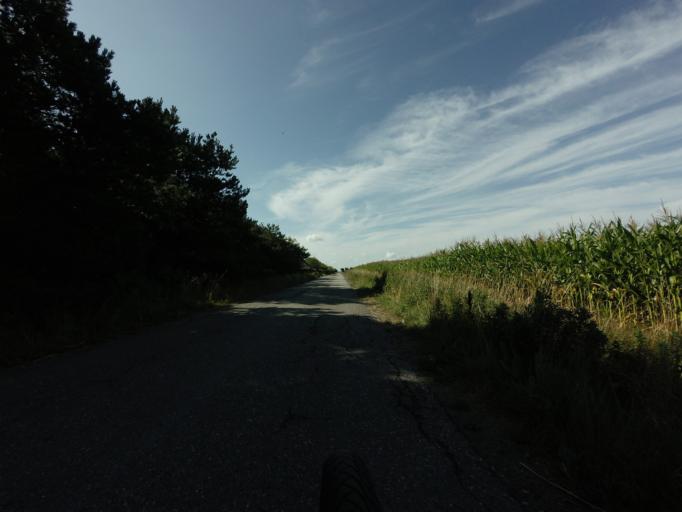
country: DK
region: North Denmark
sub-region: Hjorring Kommune
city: Vra
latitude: 57.4032
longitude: 9.9553
